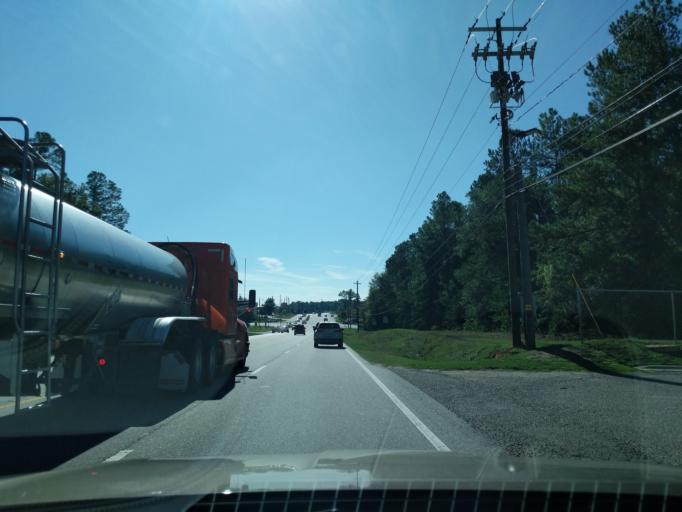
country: US
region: Georgia
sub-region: Richmond County
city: Augusta
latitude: 33.3712
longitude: -81.9982
